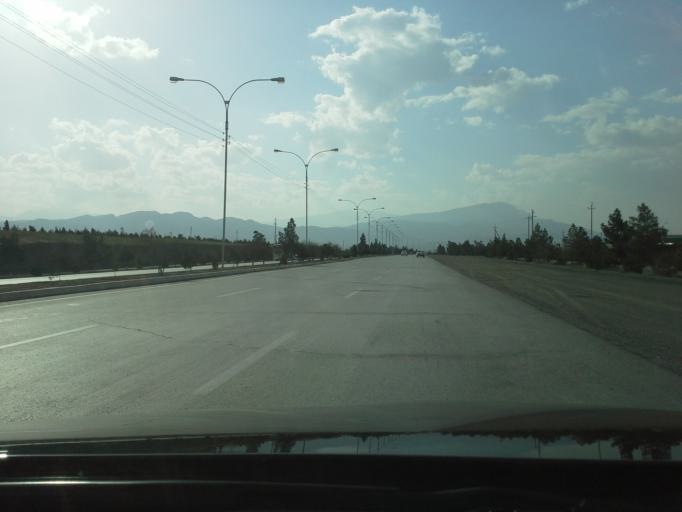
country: TM
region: Ahal
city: Abadan
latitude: 37.9708
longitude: 58.2687
